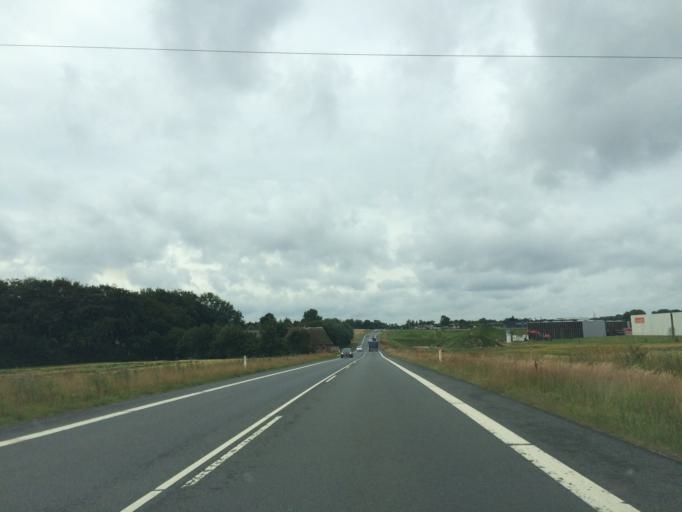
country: DK
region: Central Jutland
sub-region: Silkeborg Kommune
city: Silkeborg
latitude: 56.2072
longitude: 9.6043
